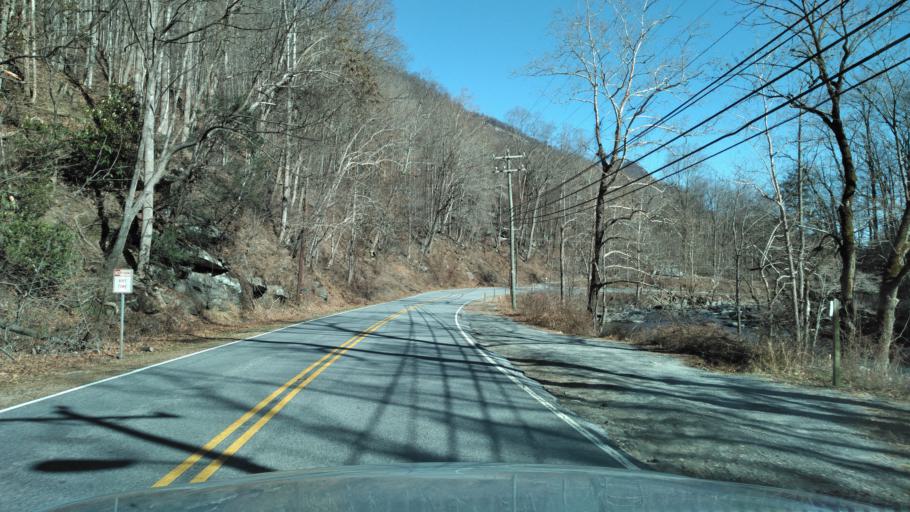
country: US
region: North Carolina
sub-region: Rutherford County
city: Lake Lure
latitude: 35.4456
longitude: -82.2731
